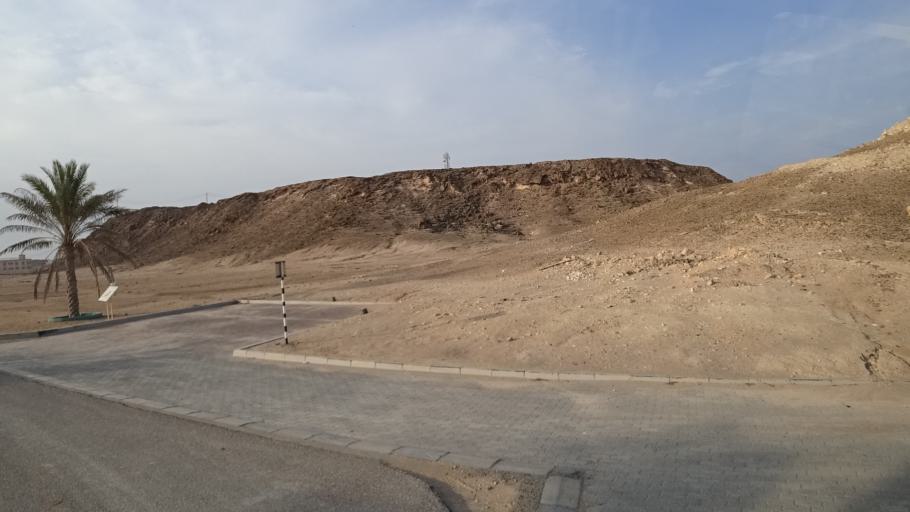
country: OM
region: Ash Sharqiyah
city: Sur
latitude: 22.4262
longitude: 59.8270
